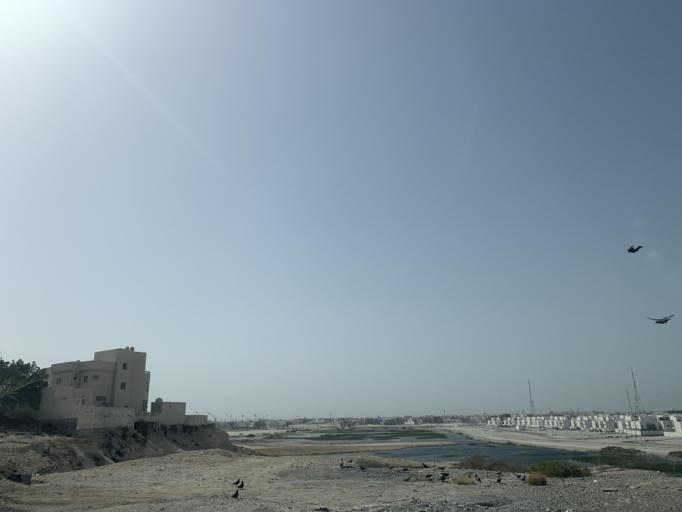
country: BH
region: Northern
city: Ar Rifa'
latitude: 26.1455
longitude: 50.5662
